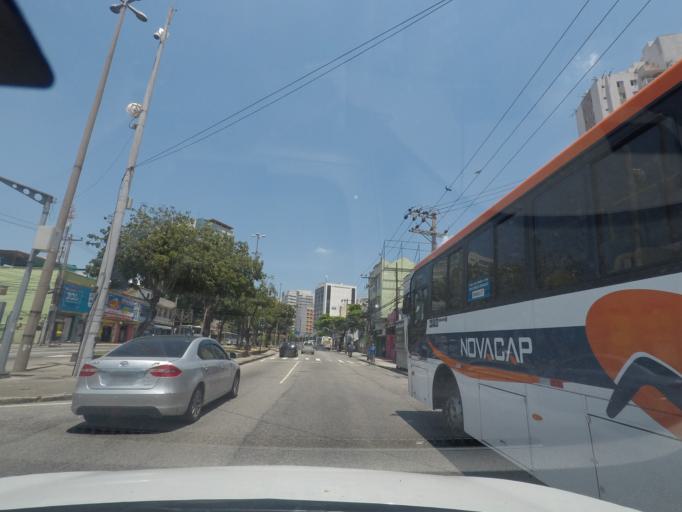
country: BR
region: Rio de Janeiro
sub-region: Rio De Janeiro
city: Rio de Janeiro
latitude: -22.8871
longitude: -43.2873
